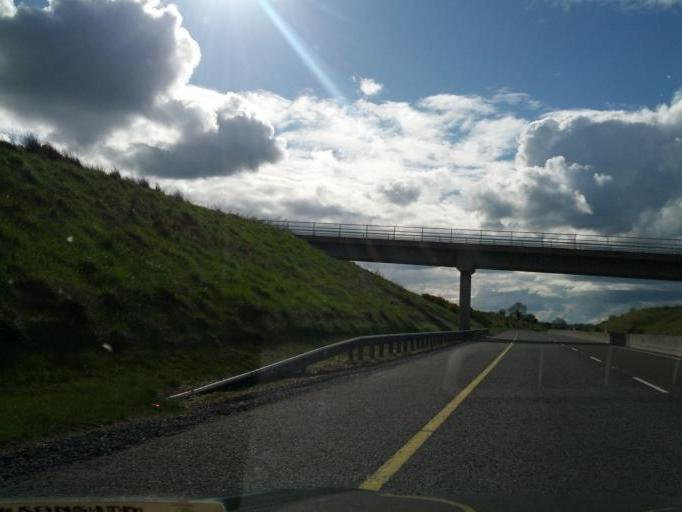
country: IE
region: Leinster
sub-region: Uibh Fhaili
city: Clara
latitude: 53.3856
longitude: -7.5919
